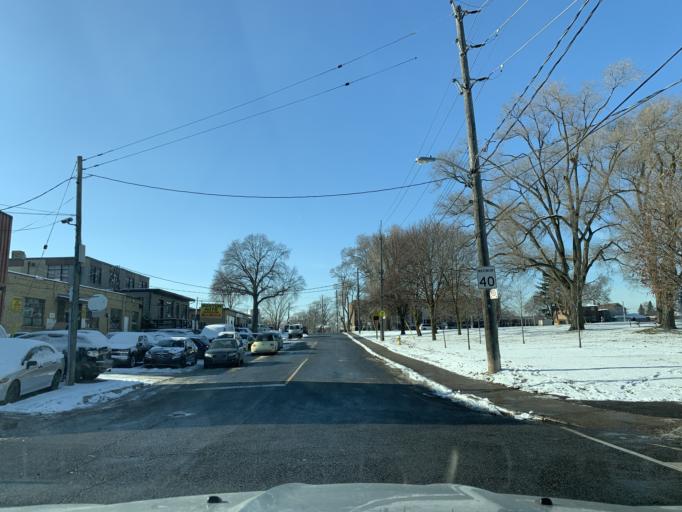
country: CA
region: Ontario
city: Toronto
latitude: 43.6762
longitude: -79.4761
